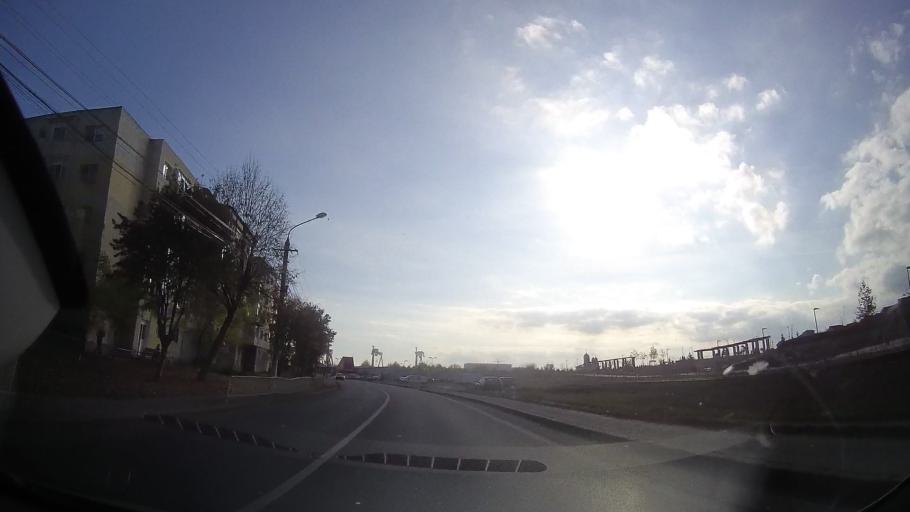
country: RO
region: Constanta
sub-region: Municipiul Mangalia
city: Mangalia
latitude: 43.8112
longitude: 28.5719
